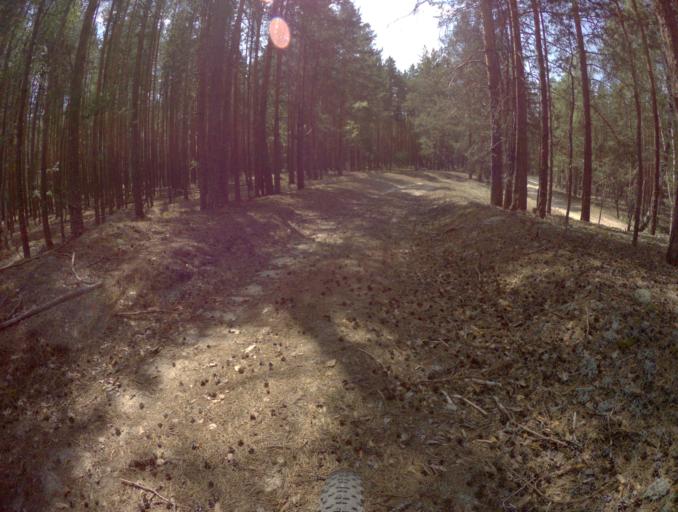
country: RU
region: Ivanovo
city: Talitsy
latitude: 56.4041
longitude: 42.3766
